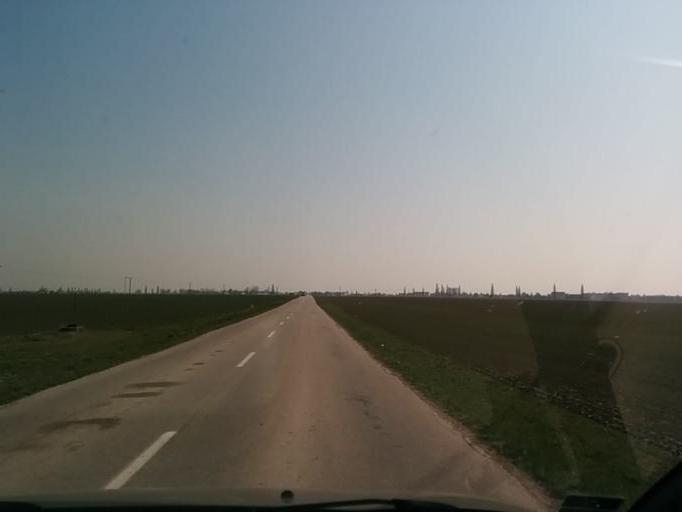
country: SK
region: Trnavsky
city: Sladkovicovo
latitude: 48.2106
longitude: 17.6133
